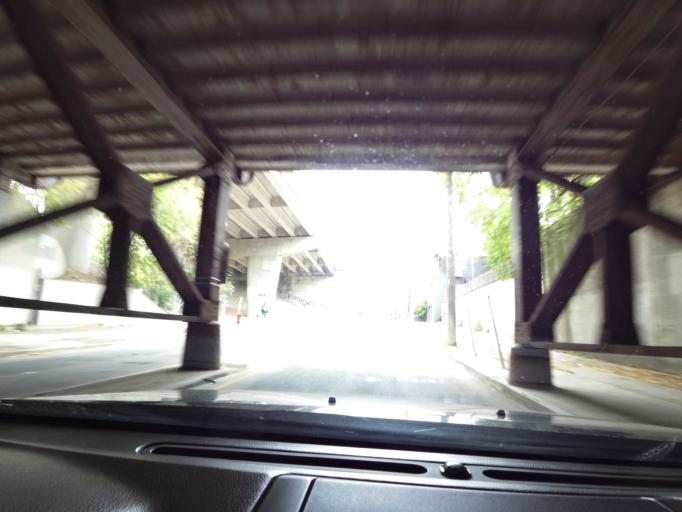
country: CA
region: Ontario
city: Hamilton
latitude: 43.2477
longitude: -79.8592
